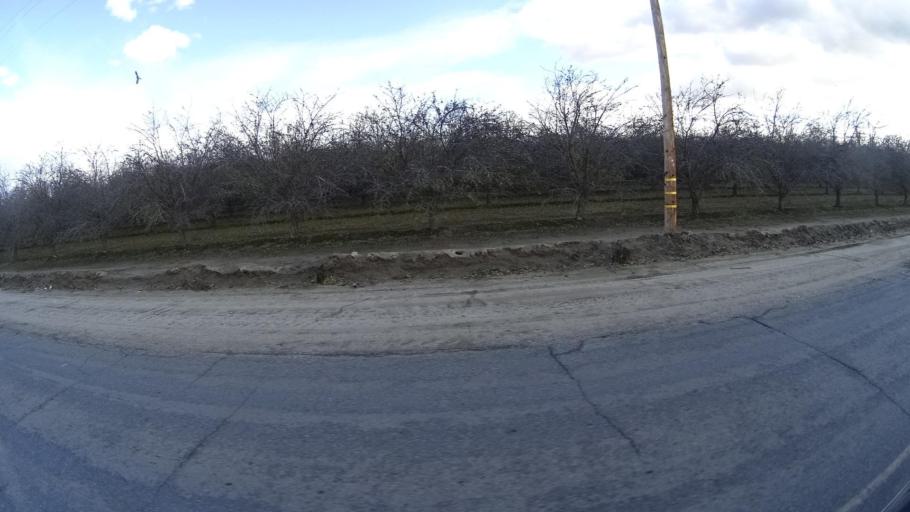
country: US
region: California
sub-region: Kern County
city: Greenfield
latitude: 35.2406
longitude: -119.0568
